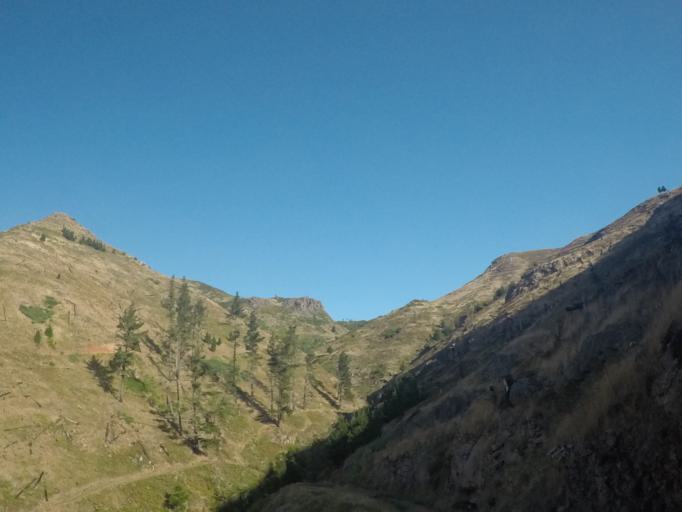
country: PT
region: Madeira
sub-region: Funchal
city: Nossa Senhora do Monte
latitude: 32.7087
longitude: -16.9010
